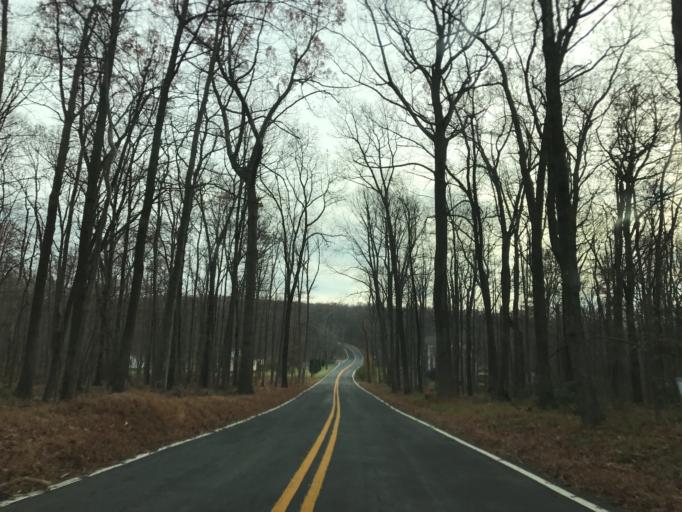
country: US
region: Maryland
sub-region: Frederick County
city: Myersville
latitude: 39.5508
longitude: -77.5009
